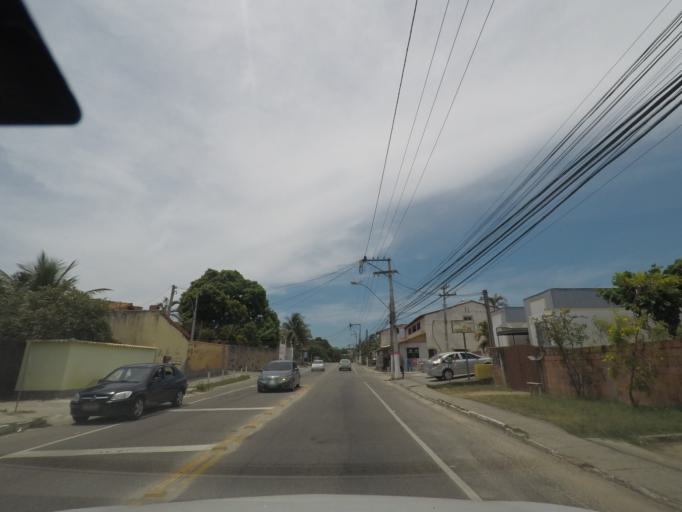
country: BR
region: Rio de Janeiro
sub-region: Marica
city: Marica
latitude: -22.9311
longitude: -42.8228
